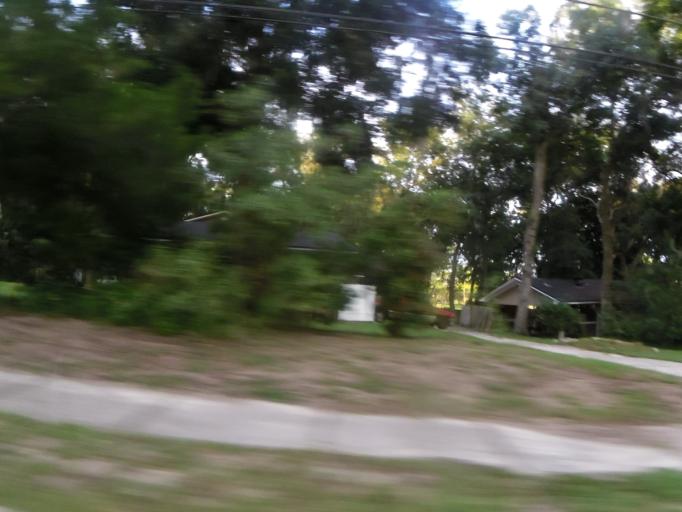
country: US
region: Florida
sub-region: Duval County
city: Atlantic Beach
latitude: 30.3784
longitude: -81.5028
